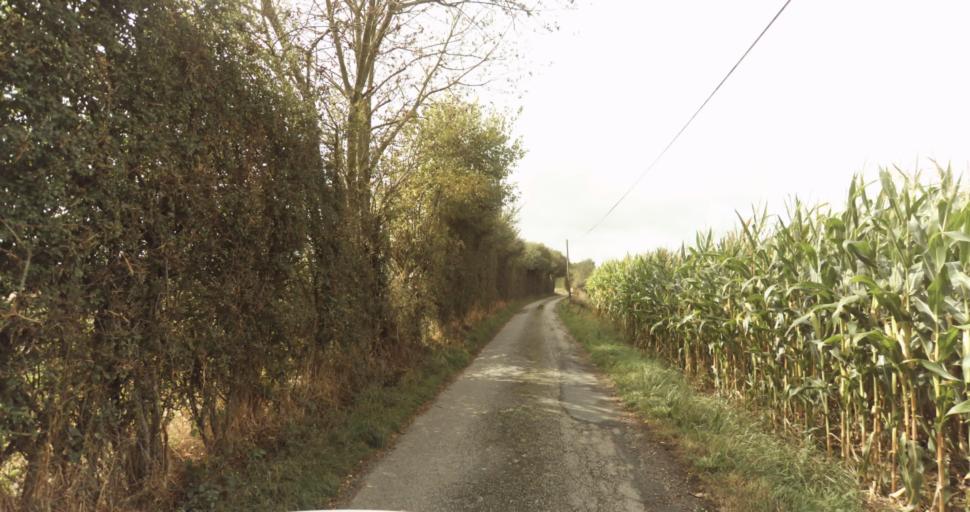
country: FR
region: Lower Normandy
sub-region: Departement de l'Orne
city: Gace
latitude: 48.8513
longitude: 0.3694
